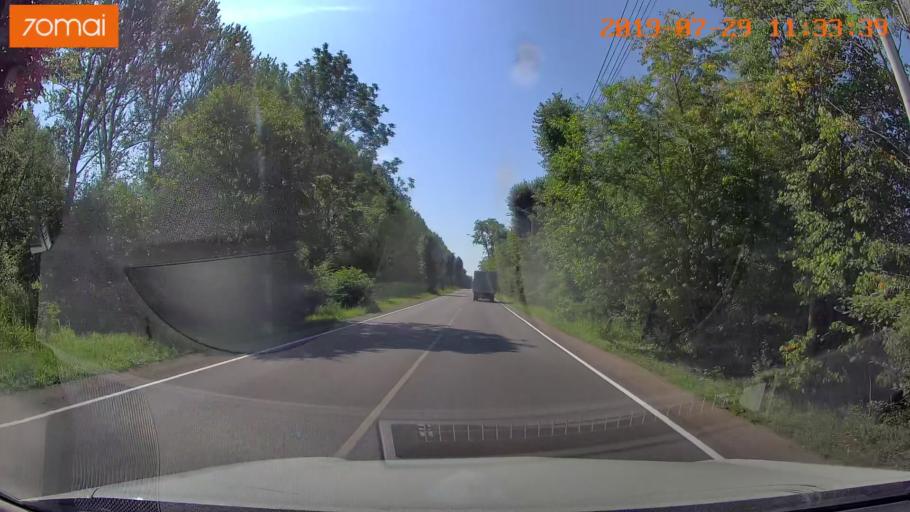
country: RU
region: Kaliningrad
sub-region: Gorod Kaliningrad
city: Kaliningrad
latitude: 54.6629
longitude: 20.5405
